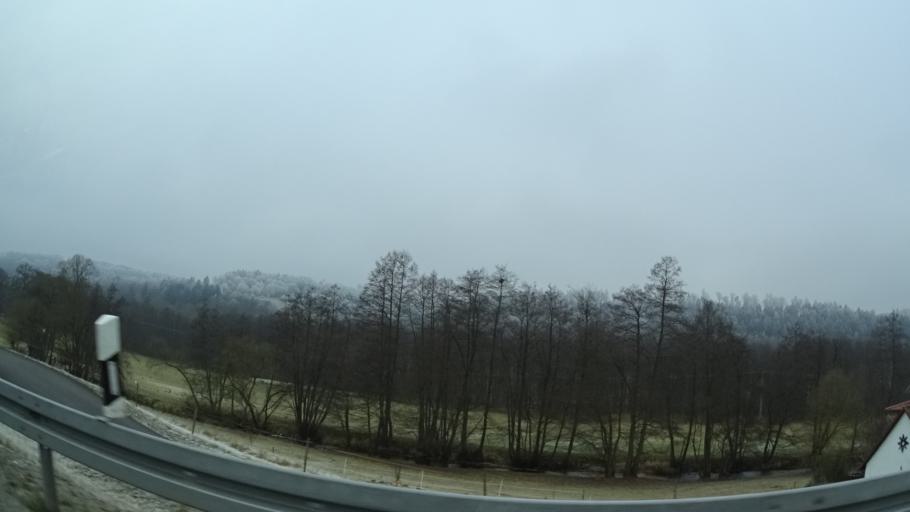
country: DE
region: Bavaria
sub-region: Regierungsbezirk Unterfranken
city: Zeitlofs
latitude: 50.2617
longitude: 9.6841
